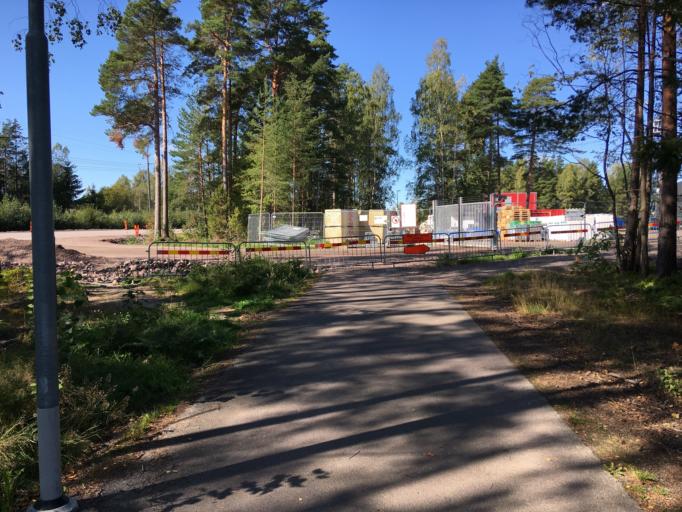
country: SE
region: Vaermland
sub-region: Karlstads Kommun
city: Karlstad
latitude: 59.3315
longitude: 13.5180
